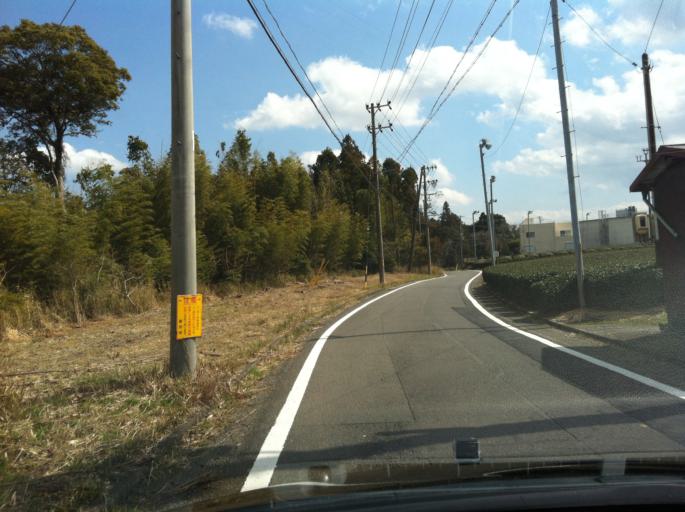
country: JP
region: Shizuoka
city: Kanaya
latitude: 34.8157
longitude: 138.1200
